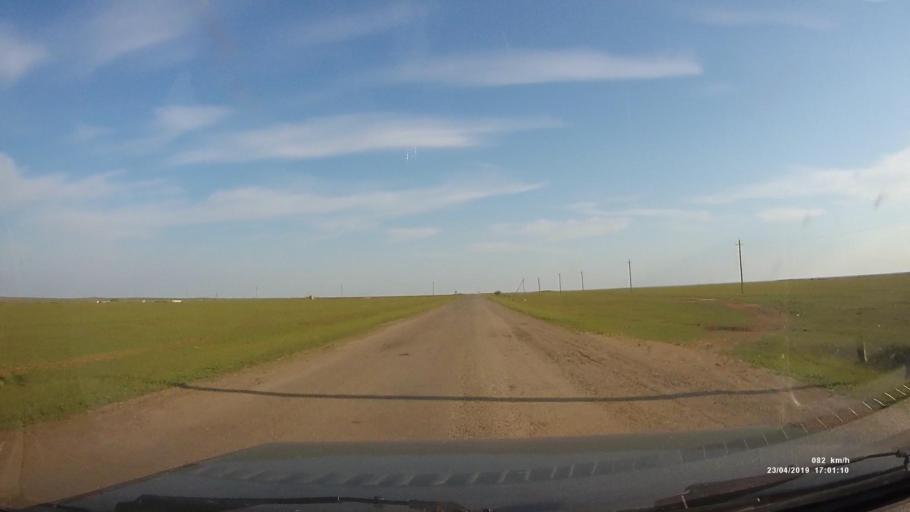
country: RU
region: Kalmykiya
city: Priyutnoye
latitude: 46.2987
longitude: 43.4073
